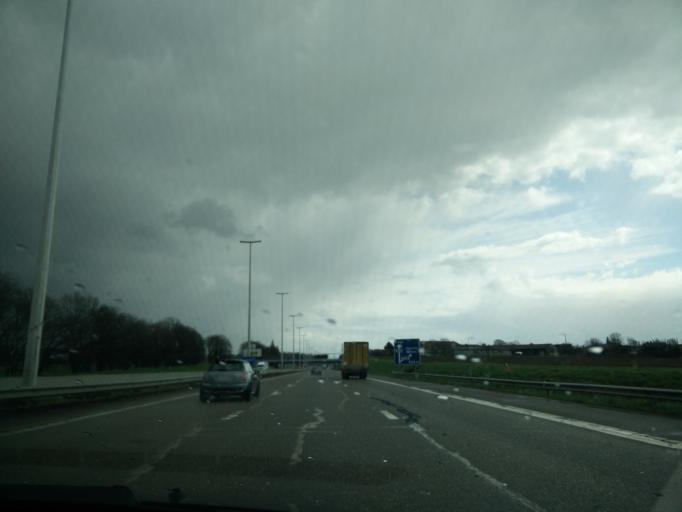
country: BE
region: Wallonia
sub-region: Province de Liege
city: Awans
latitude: 50.6807
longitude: 5.4463
